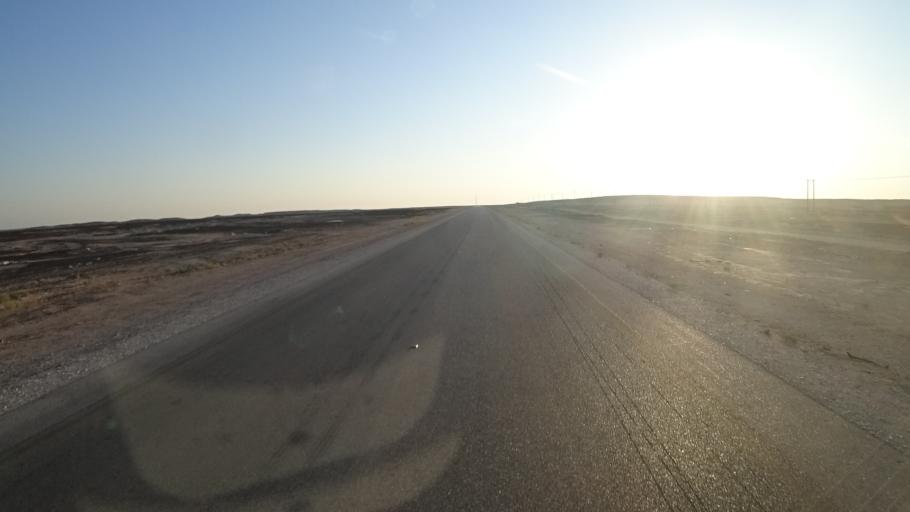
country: OM
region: Zufar
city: Salalah
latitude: 17.5513
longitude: 53.4290
